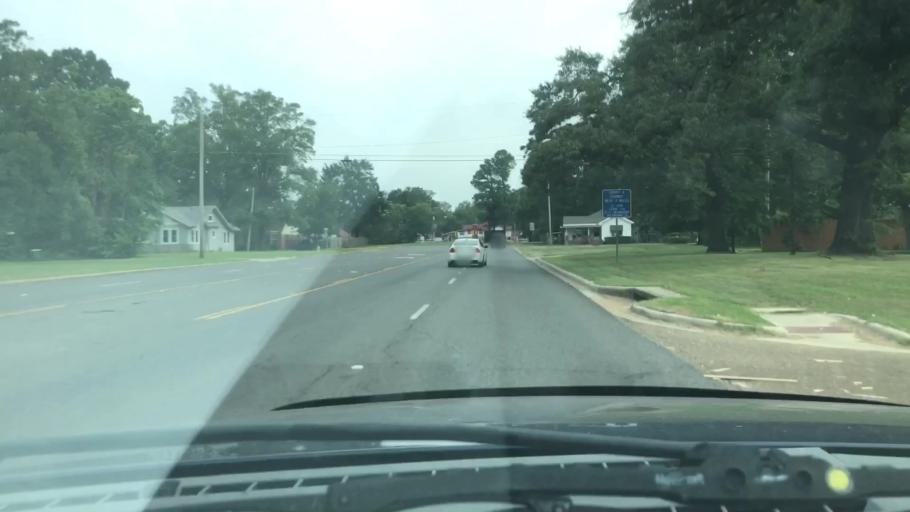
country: US
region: Texas
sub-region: Bowie County
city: Texarkana
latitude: 33.4308
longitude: -94.0615
